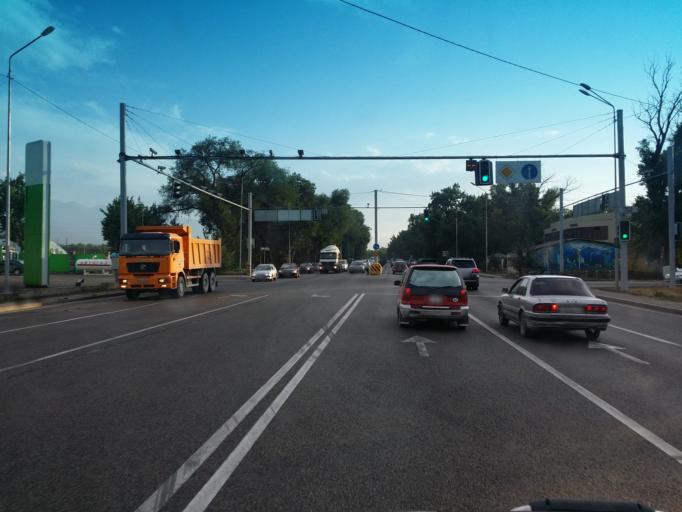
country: KZ
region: Almaty Qalasy
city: Almaty
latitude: 43.2958
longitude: 76.9981
